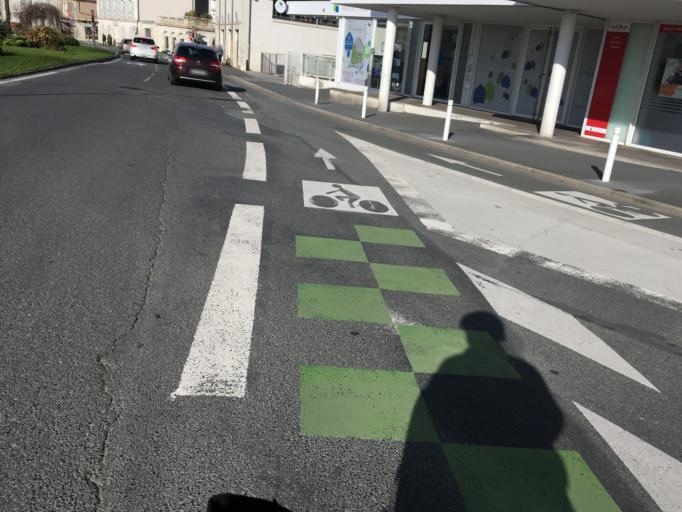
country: FR
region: Poitou-Charentes
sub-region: Departement de la Charente-Maritime
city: La Rochelle
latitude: 46.1585
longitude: -1.1455
